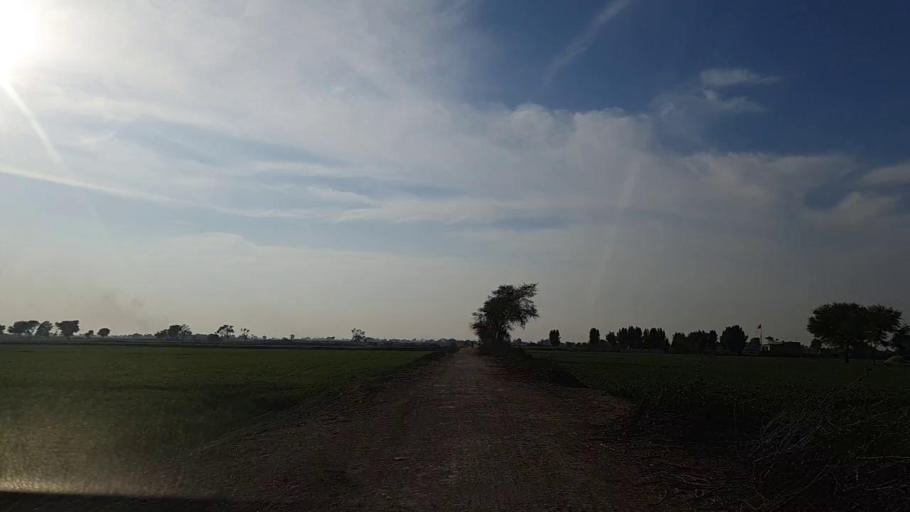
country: PK
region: Sindh
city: Bandhi
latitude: 26.5531
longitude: 68.2606
